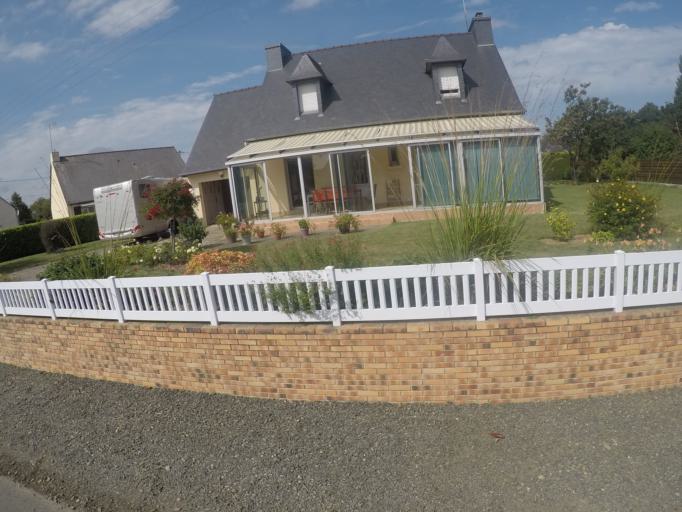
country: FR
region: Brittany
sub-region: Departement des Cotes-d'Armor
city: Goudelin
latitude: 48.6032
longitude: -3.0135
